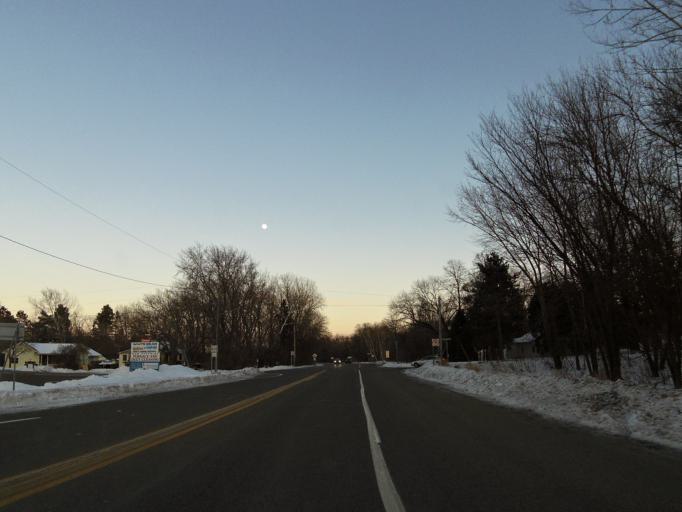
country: US
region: Minnesota
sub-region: Ramsey County
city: White Bear Lake
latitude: 45.0934
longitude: -93.0056
